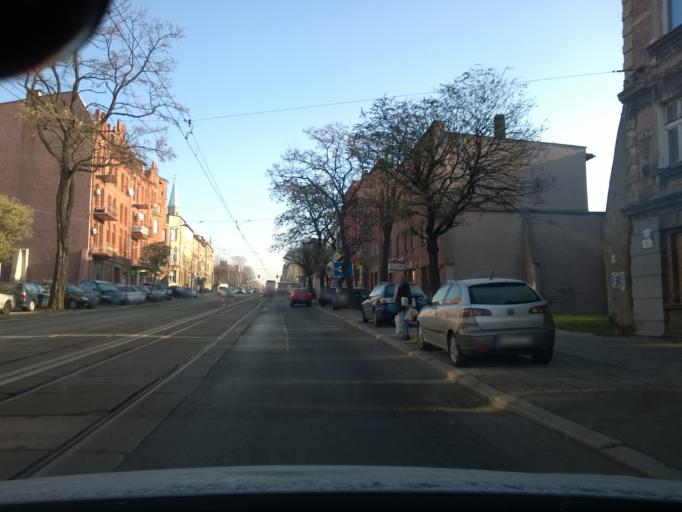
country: PL
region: Silesian Voivodeship
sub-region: Swietochlowice
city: Swietochlowice
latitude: 50.3028
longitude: 18.9423
